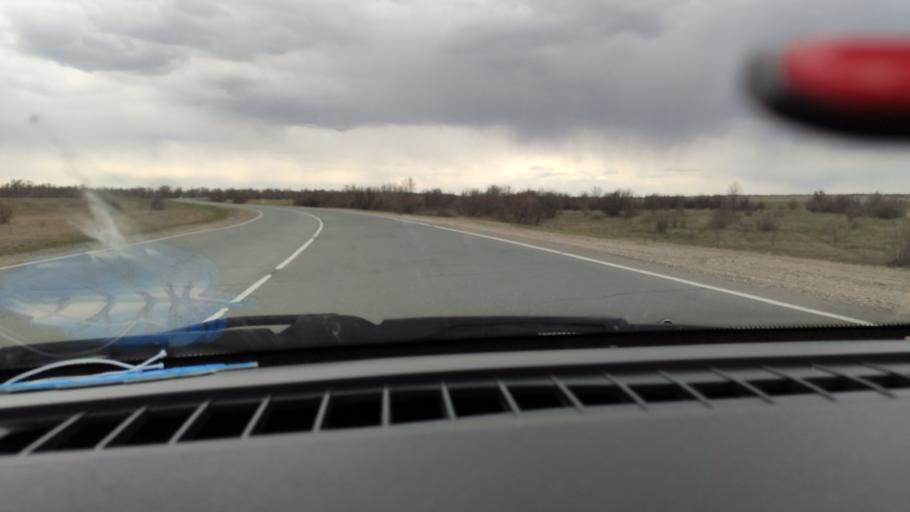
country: RU
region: Saratov
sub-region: Saratovskiy Rayon
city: Saratov
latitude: 51.7178
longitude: 46.0264
